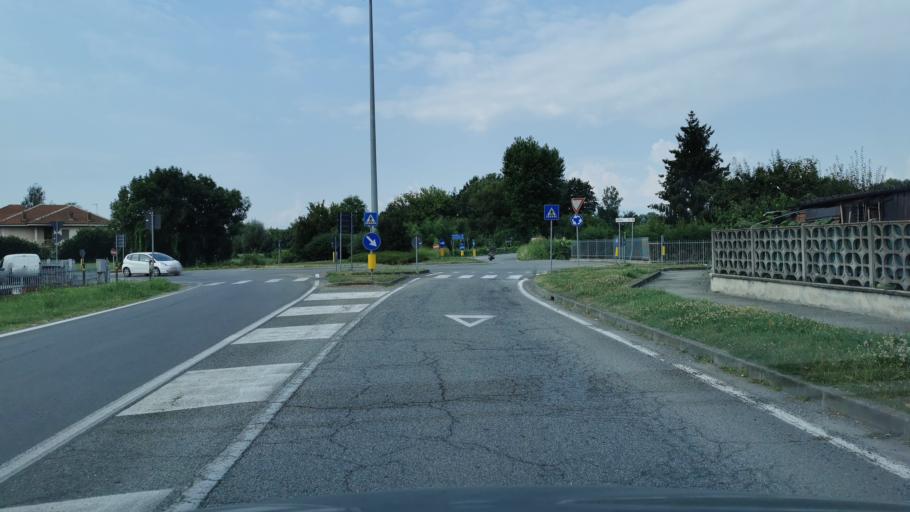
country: IT
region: Piedmont
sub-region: Provincia di Torino
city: Airasca
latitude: 44.9159
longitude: 7.4906
